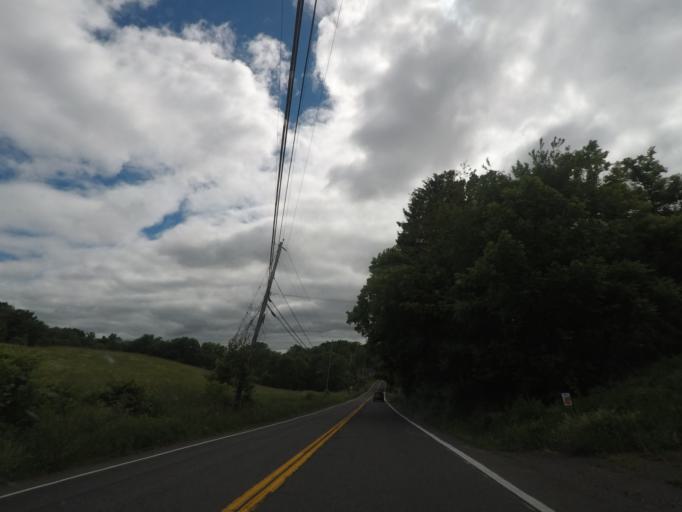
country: US
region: New York
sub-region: Columbia County
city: Philmont
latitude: 42.2268
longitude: -73.7126
